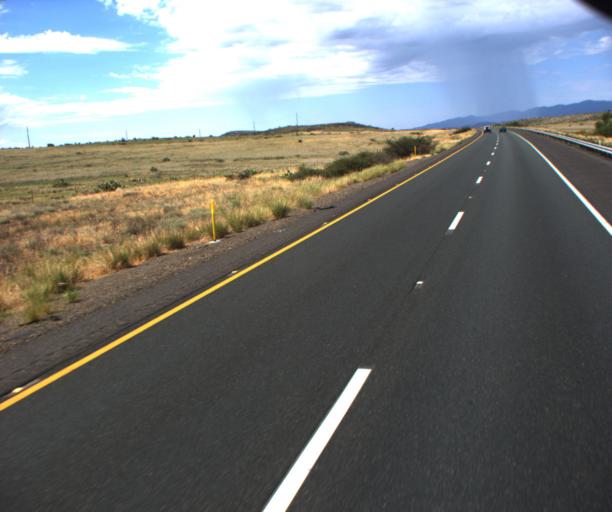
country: US
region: Arizona
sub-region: Yavapai County
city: Cordes Lakes
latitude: 34.4374
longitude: -112.0439
